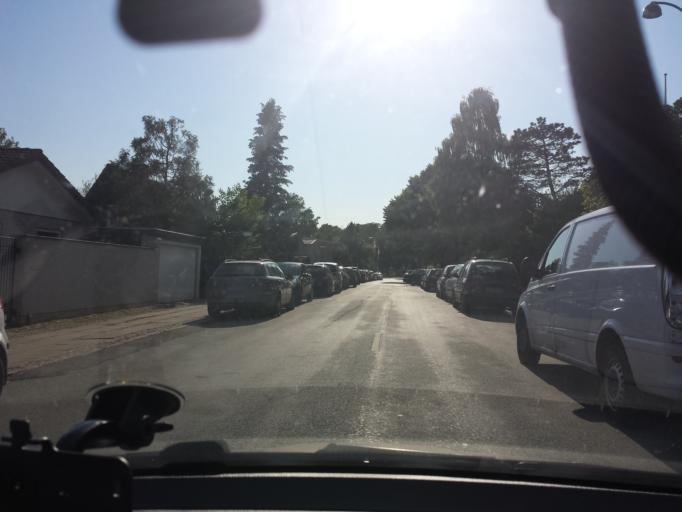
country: DK
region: Capital Region
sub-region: Gentofte Kommune
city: Charlottenlund
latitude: 55.7748
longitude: 12.5819
